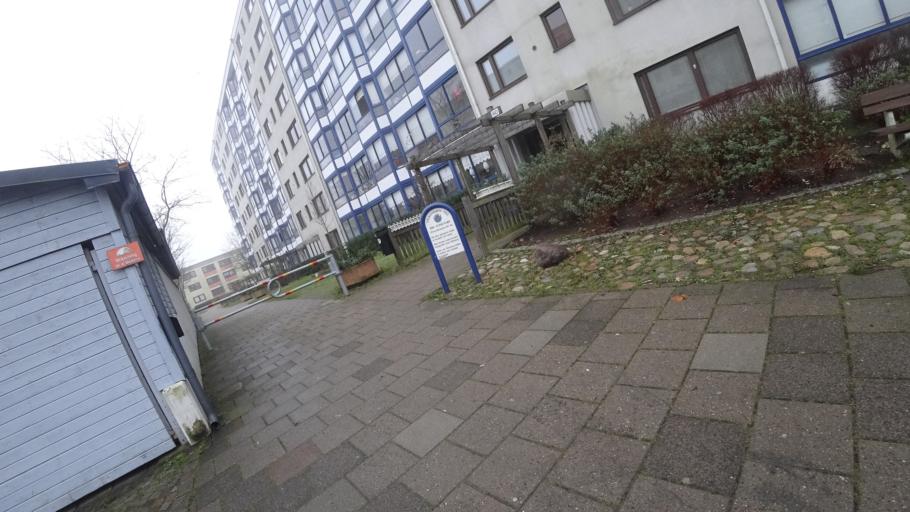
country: SE
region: Skane
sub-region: Malmo
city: Malmoe
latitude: 55.5666
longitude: 13.0081
